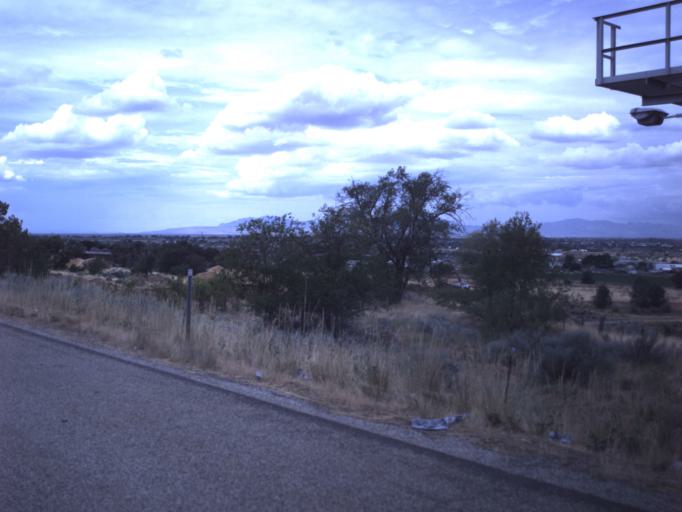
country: US
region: Utah
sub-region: Weber County
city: Riverdale
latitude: 41.2014
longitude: -112.0177
